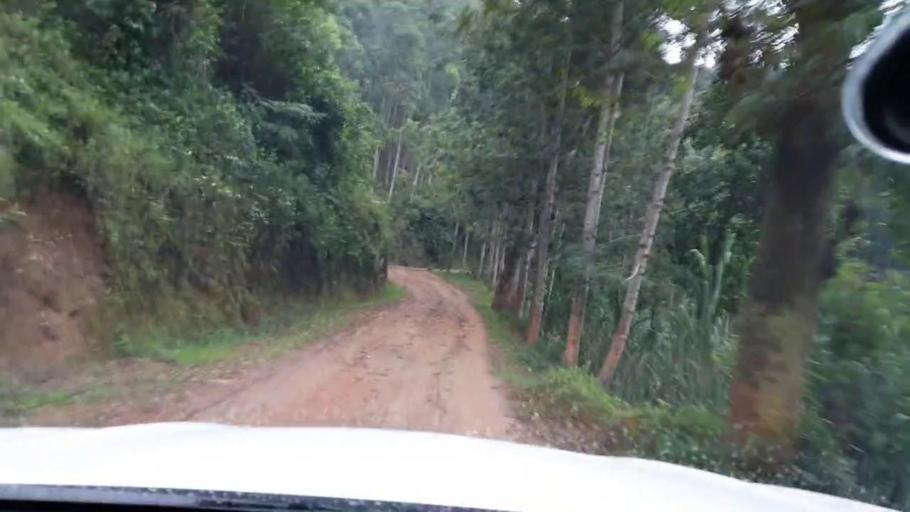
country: RW
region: Western Province
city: Cyangugu
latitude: -2.4121
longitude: 29.1924
